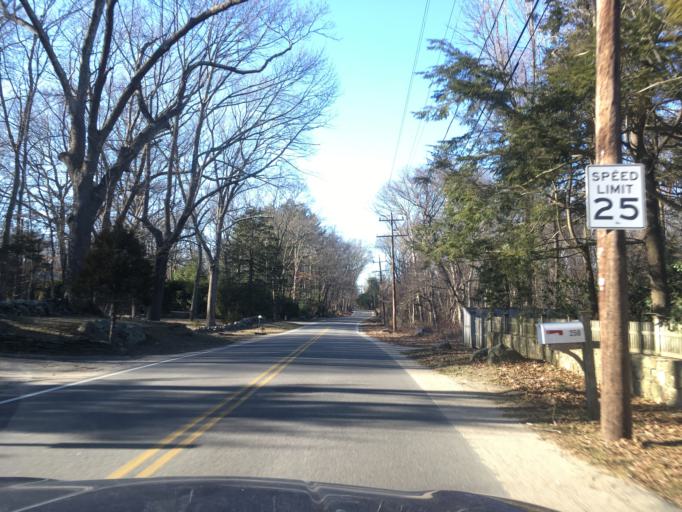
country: US
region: Rhode Island
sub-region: Kent County
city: East Greenwich
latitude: 41.6565
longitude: -71.4762
